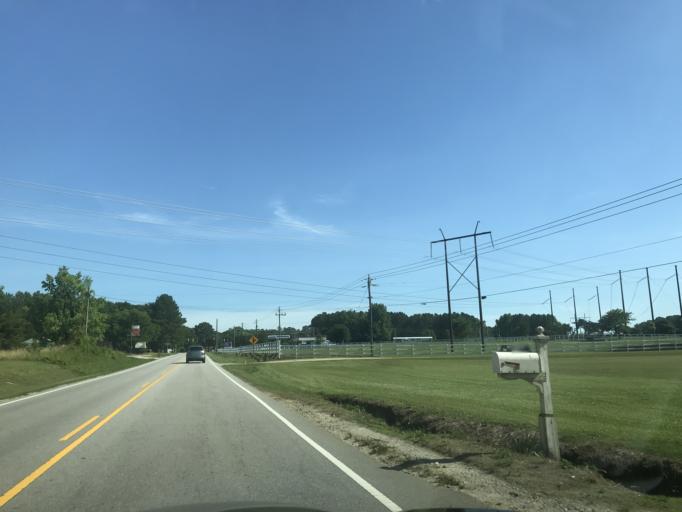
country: US
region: North Carolina
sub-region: Wake County
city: Garner
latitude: 35.6730
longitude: -78.5761
